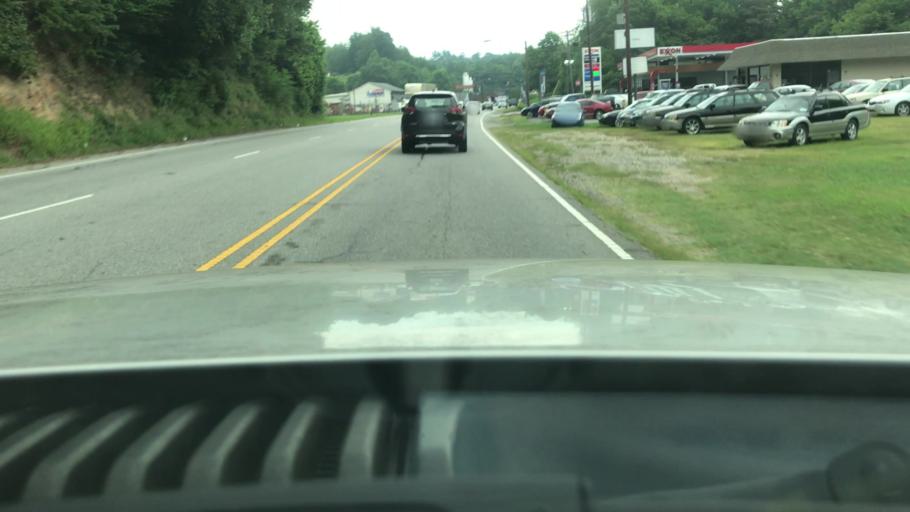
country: US
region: North Carolina
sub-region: Wilkes County
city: Wilkesboro
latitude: 36.1526
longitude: -81.1752
